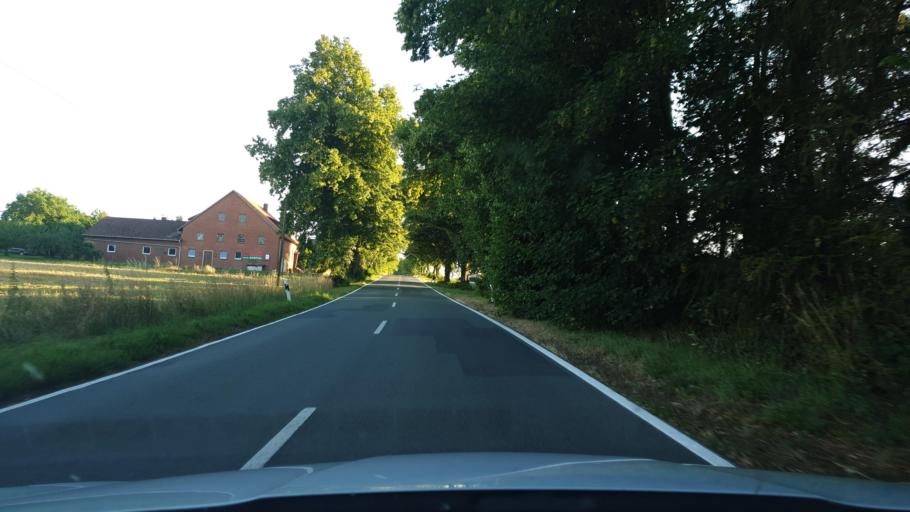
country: DE
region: Lower Saxony
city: Apelern
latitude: 52.2769
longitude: 9.2963
